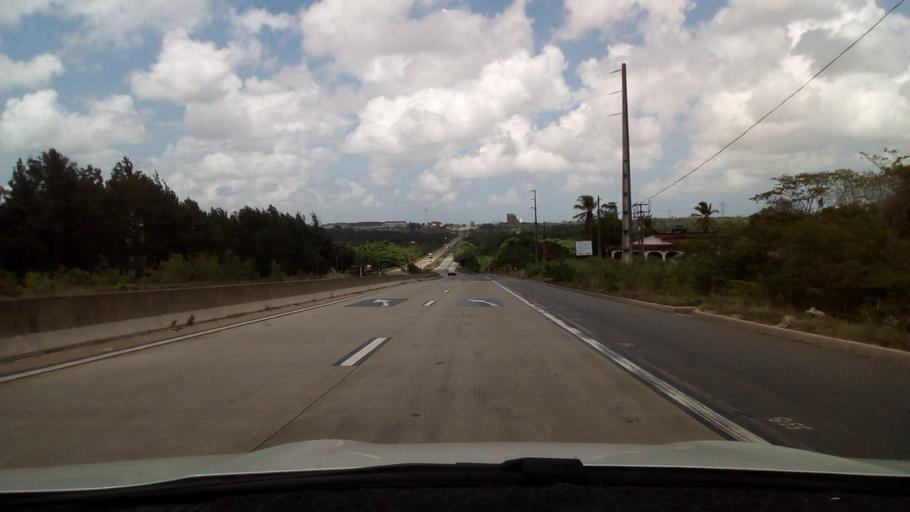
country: BR
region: Paraiba
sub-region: Conde
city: Conde
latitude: -7.2217
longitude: -34.9138
